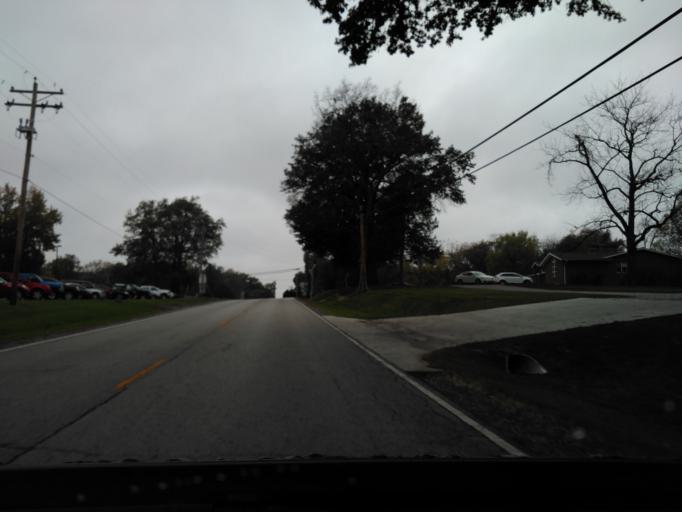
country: US
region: Illinois
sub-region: Bond County
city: Greenville
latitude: 38.9019
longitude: -89.3990
